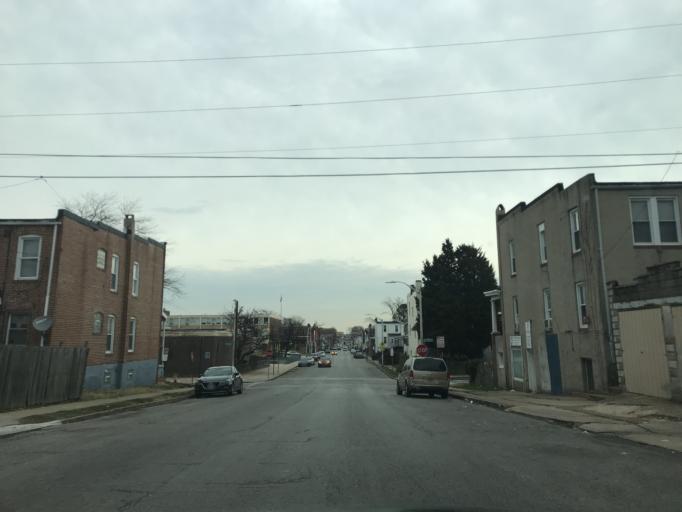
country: US
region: Maryland
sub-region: City of Baltimore
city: Baltimore
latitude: 39.3065
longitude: -76.6519
